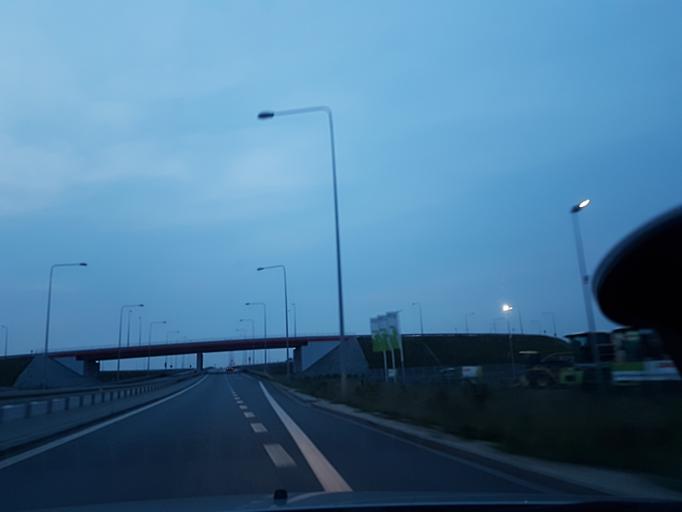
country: PL
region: Lodz Voivodeship
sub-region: Powiat kutnowski
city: Krzyzanow
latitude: 52.2195
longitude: 19.4664
